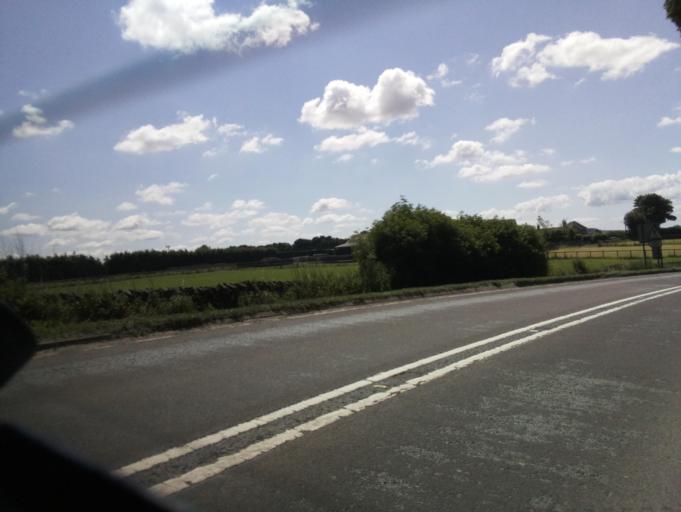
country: GB
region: England
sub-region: Derbyshire
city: Buxton
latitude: 53.2717
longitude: -1.8936
